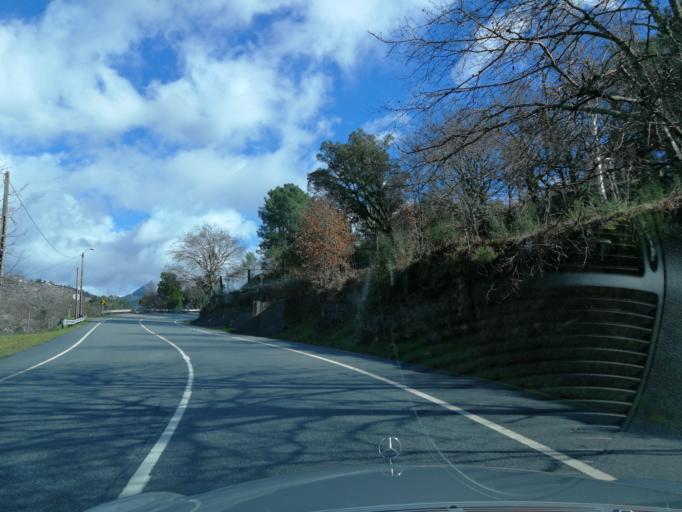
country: ES
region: Galicia
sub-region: Provincia de Ourense
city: Entrimo
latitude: 41.8656
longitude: -8.2114
